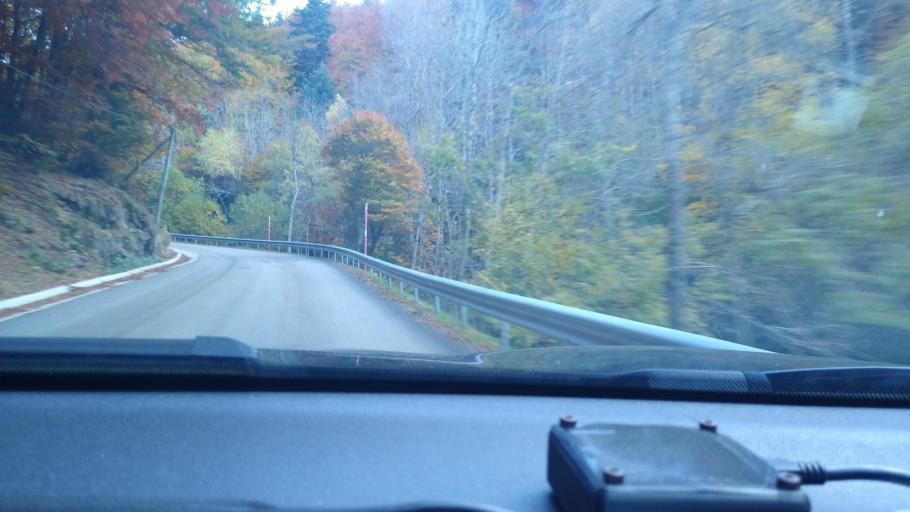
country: FR
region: Midi-Pyrenees
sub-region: Departement de l'Ariege
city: Ax-les-Thermes
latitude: 42.7172
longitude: 1.9161
